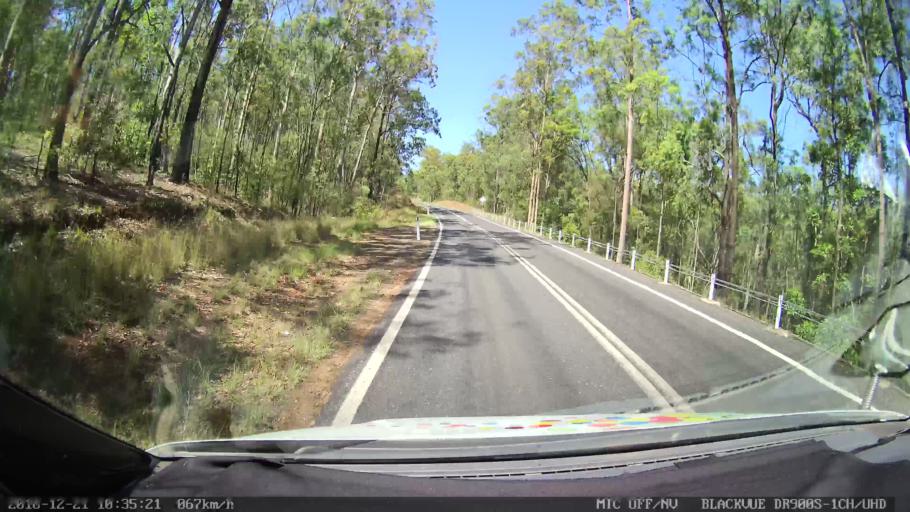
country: AU
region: New South Wales
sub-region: Clarence Valley
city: South Grafton
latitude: -29.6188
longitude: 152.6450
